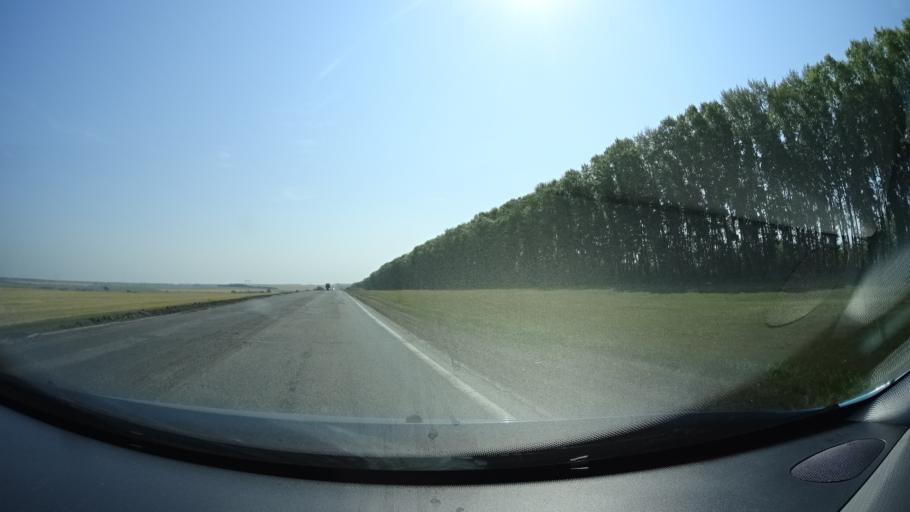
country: RU
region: Bashkortostan
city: Kabakovo
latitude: 54.4479
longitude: 55.9810
